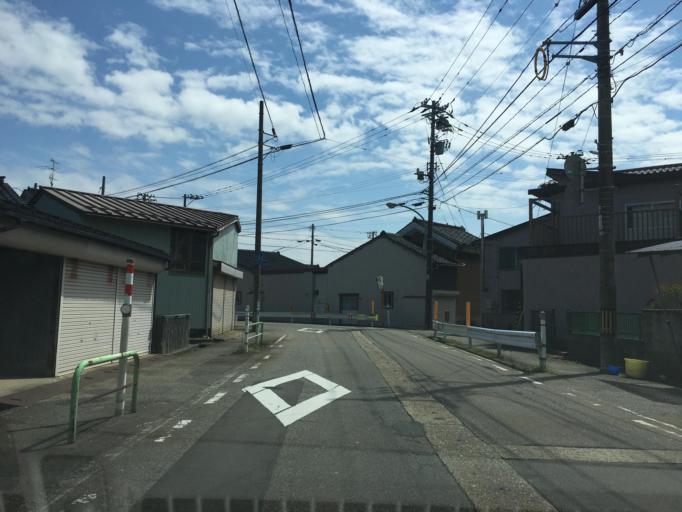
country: JP
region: Toyama
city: Nishishinminato
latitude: 36.7976
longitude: 137.0571
